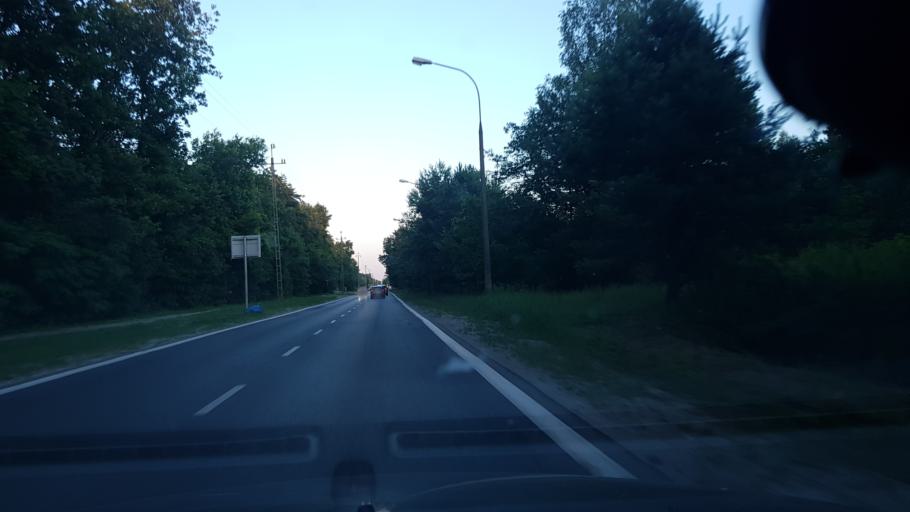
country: PL
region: Masovian Voivodeship
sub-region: Warszawa
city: Wawer
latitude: 52.1774
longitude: 21.1961
